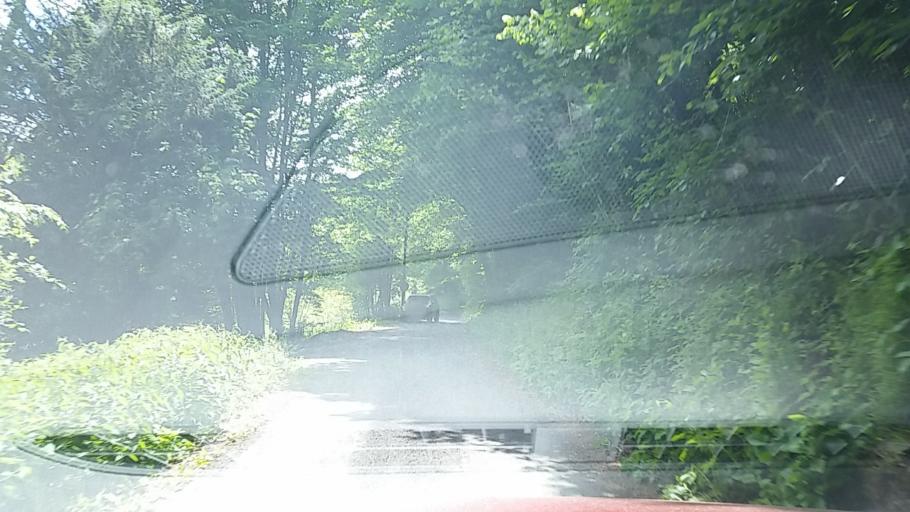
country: DE
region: Bavaria
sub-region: Regierungsbezirk Unterfranken
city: Neuendorf
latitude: 50.0186
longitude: 9.6608
